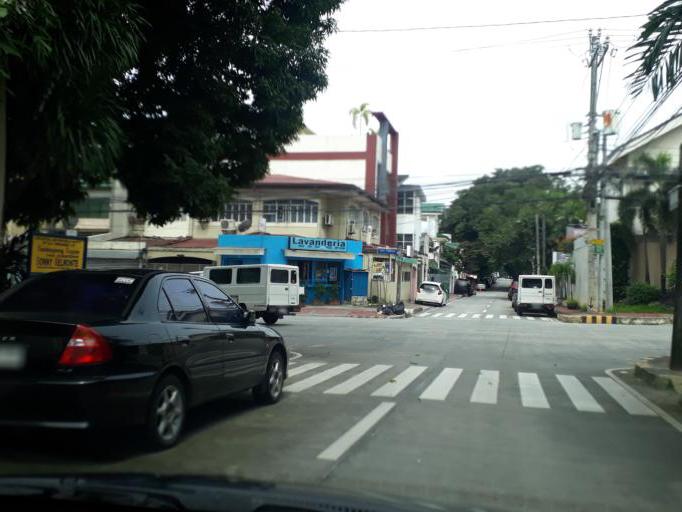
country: PH
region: Calabarzon
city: Del Monte
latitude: 14.6336
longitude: 121.0309
